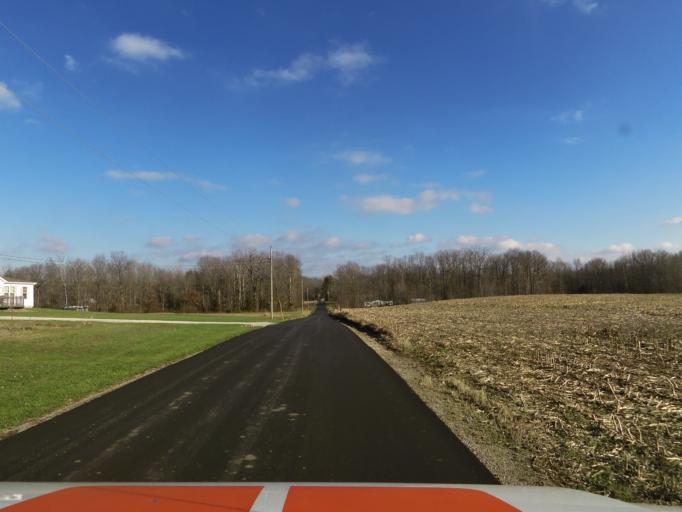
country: US
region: Indiana
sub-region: Jackson County
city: Seymour
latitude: 38.9829
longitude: -85.7950
